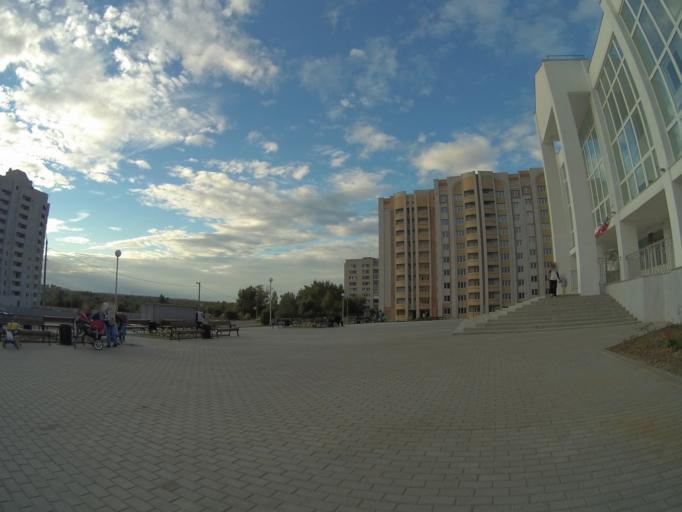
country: RU
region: Vladimir
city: Raduzhnyy
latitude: 56.1085
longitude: 40.2793
